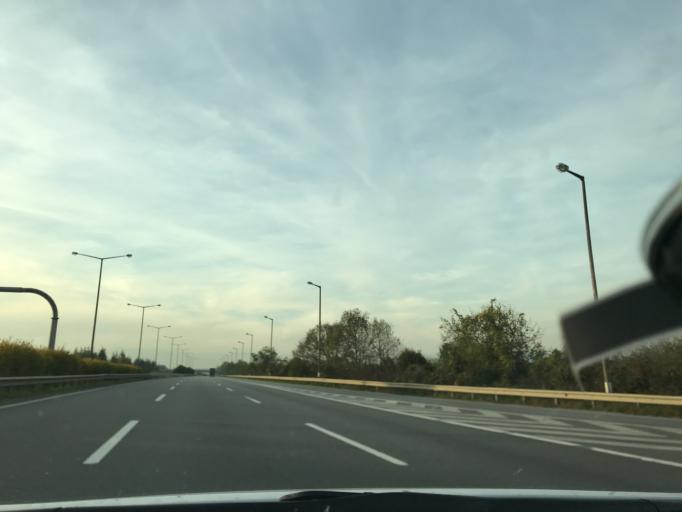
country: TR
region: Duzce
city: Cilimli
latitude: 40.8329
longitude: 31.0390
